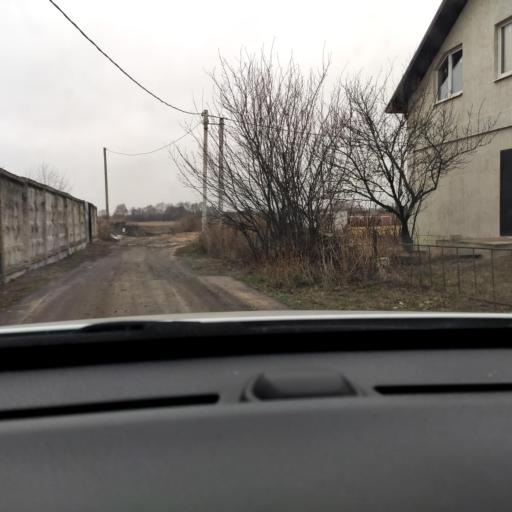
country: RU
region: Voronezj
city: Somovo
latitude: 51.6860
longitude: 39.3574
